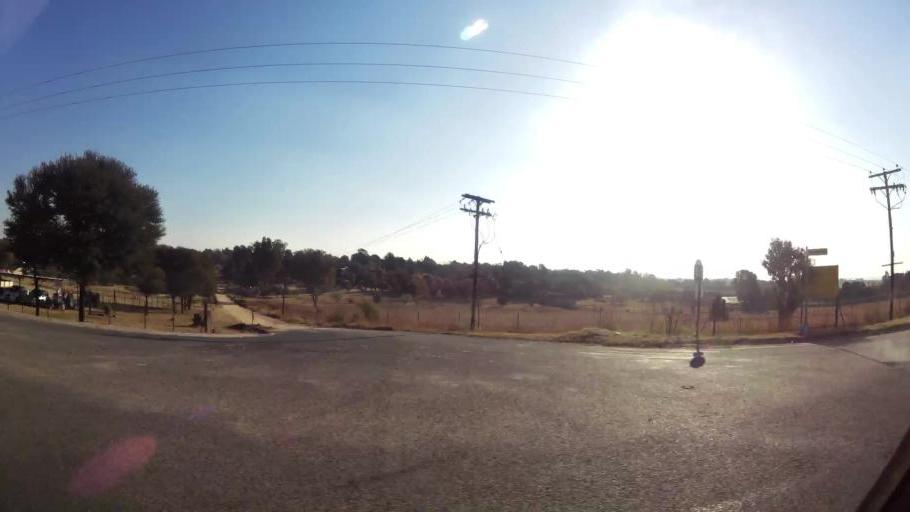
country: ZA
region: Gauteng
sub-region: West Rand District Municipality
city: Muldersdriseloop
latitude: -26.0378
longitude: 27.9099
